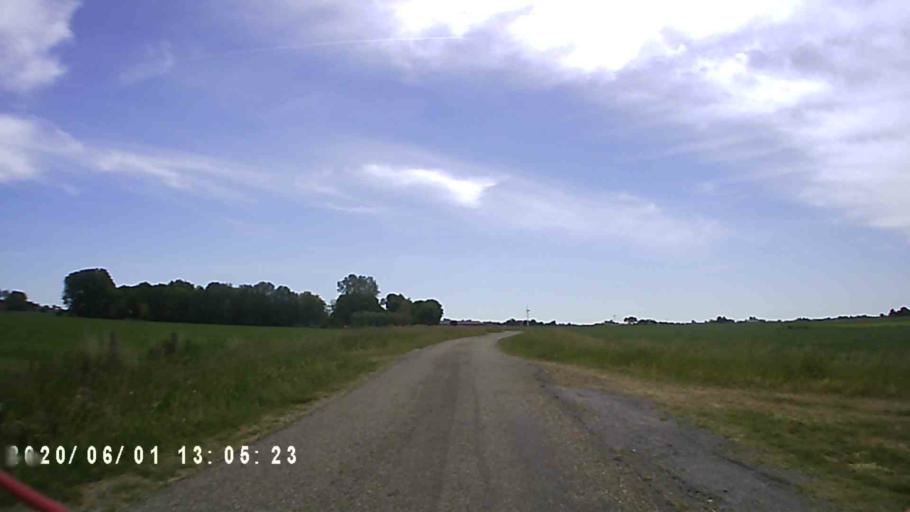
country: NL
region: Friesland
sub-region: Gemeente Franekeradeel
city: Tzum
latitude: 53.1370
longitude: 5.5476
